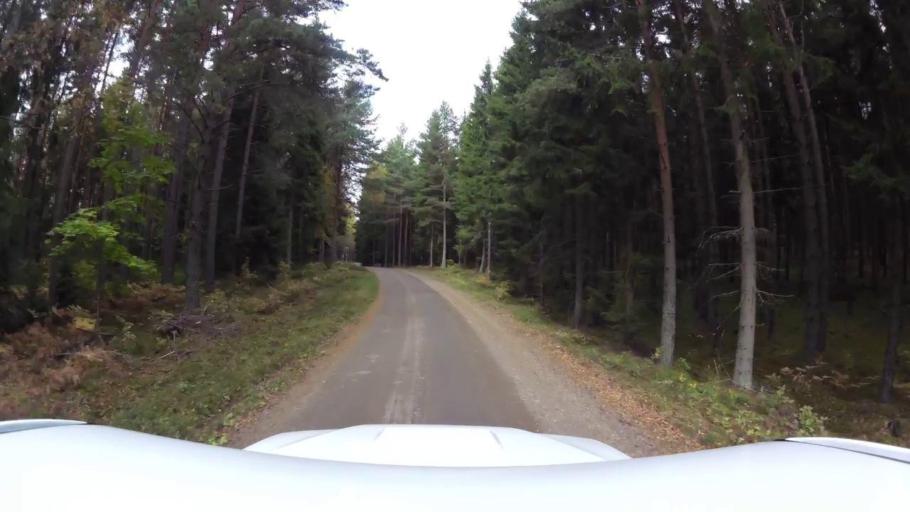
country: SE
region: OEstergoetland
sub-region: Linkopings Kommun
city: Ekangen
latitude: 58.5505
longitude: 15.6744
